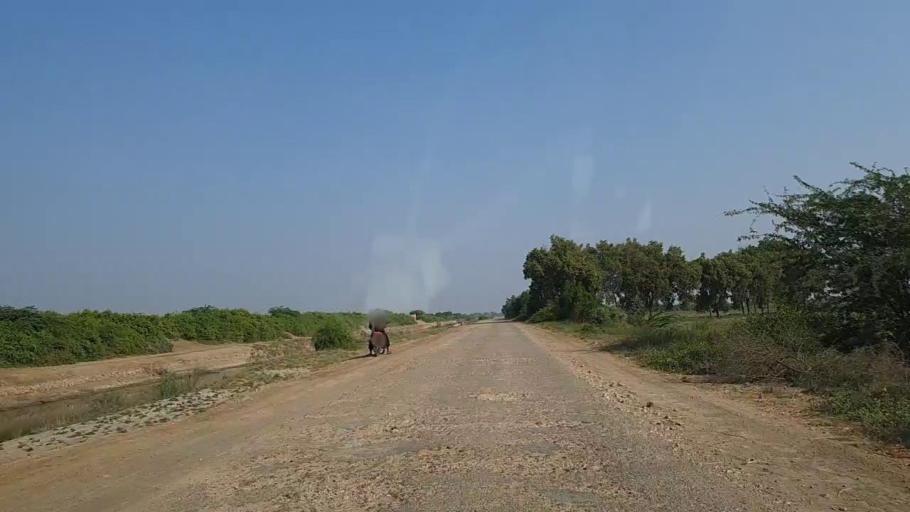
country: PK
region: Sindh
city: Mirpur Sakro
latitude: 24.6318
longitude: 67.6281
